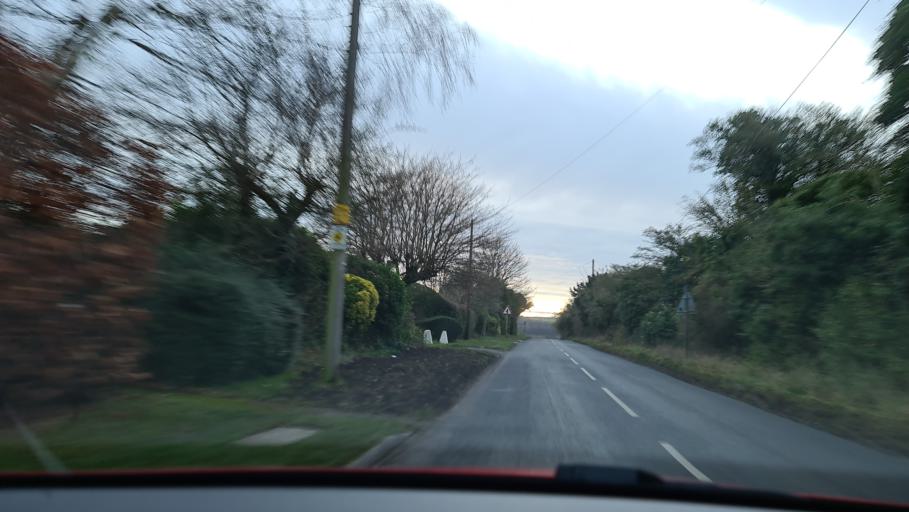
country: GB
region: England
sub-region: Buckinghamshire
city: Princes Risborough
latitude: 51.7204
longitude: -0.8241
